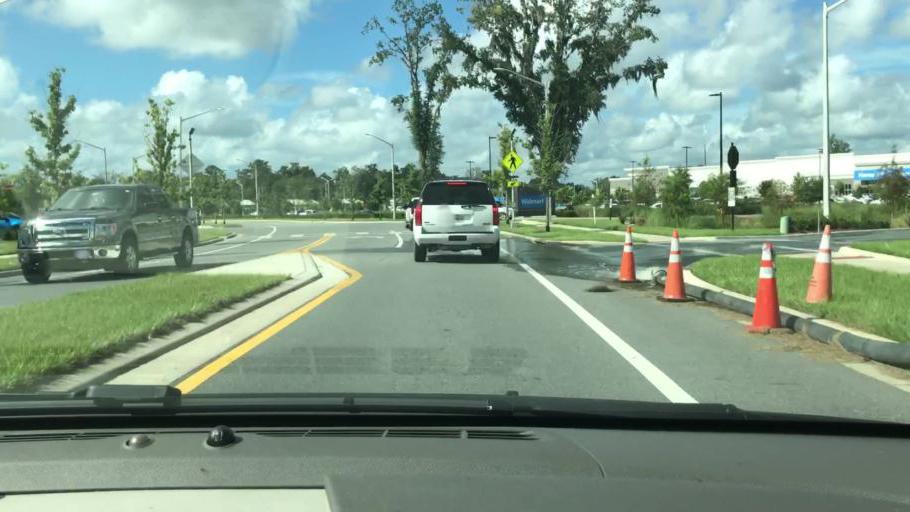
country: US
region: Florida
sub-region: Alachua County
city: Gainesville
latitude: 29.6278
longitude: -82.3865
